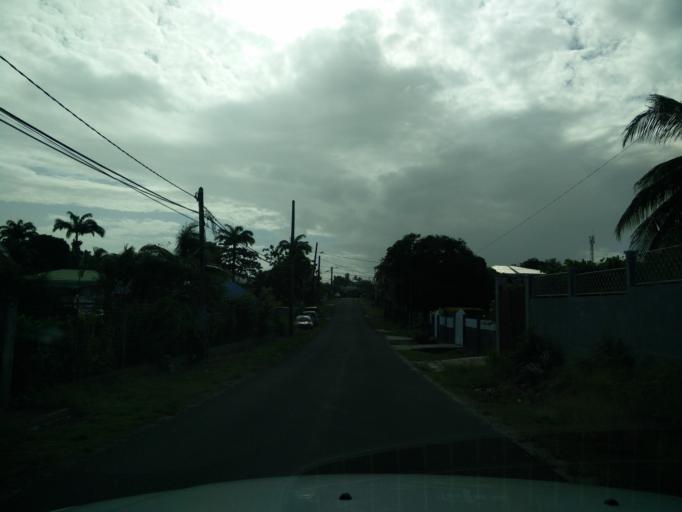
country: GP
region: Guadeloupe
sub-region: Guadeloupe
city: Sainte-Anne
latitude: 16.2313
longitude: -61.3771
